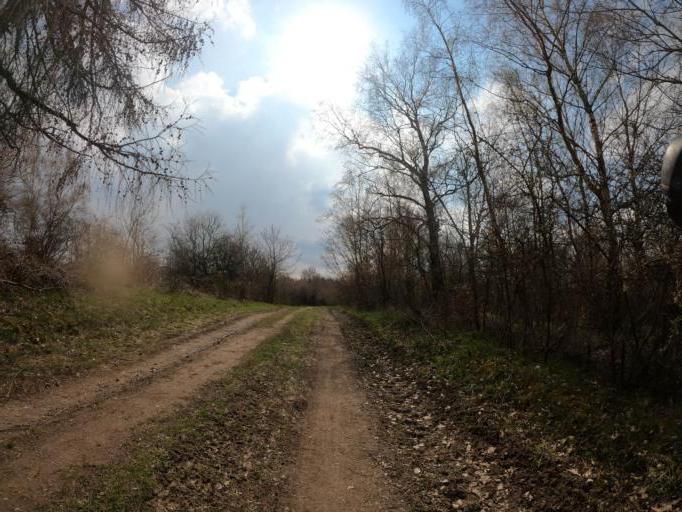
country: DE
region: North Rhine-Westphalia
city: Heimbach
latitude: 50.5917
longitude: 6.3908
